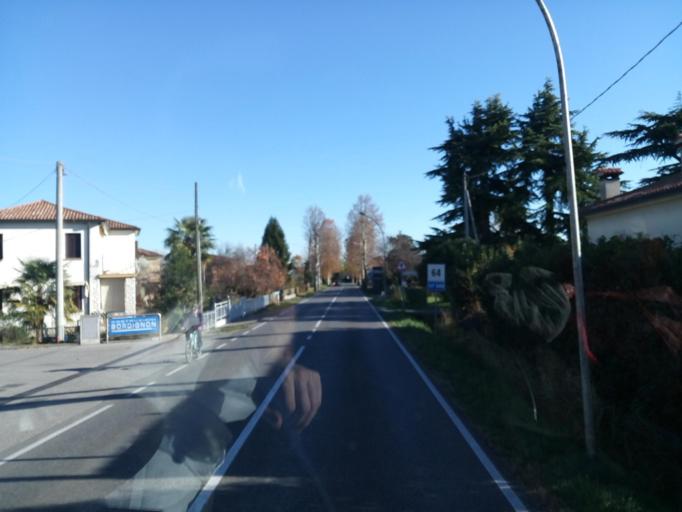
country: IT
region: Veneto
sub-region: Provincia di Treviso
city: Venegazzu
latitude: 45.7780
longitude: 12.0861
